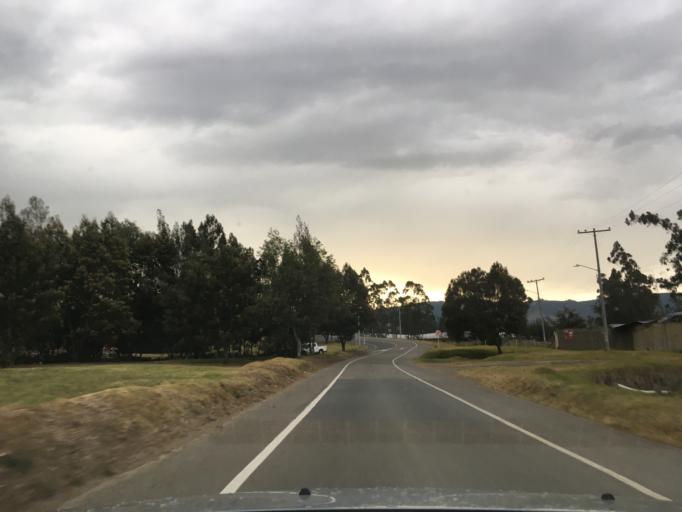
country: CO
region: Cundinamarca
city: Sesquile
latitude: 5.0564
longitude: -73.7960
